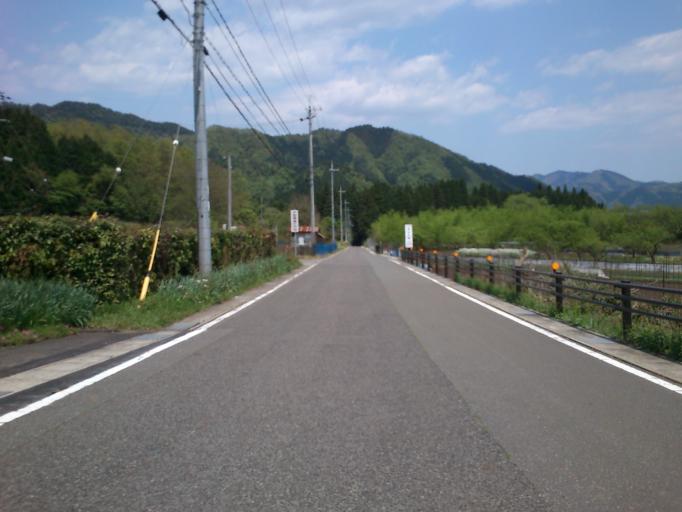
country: JP
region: Kyoto
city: Fukuchiyama
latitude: 35.3389
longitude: 134.9218
